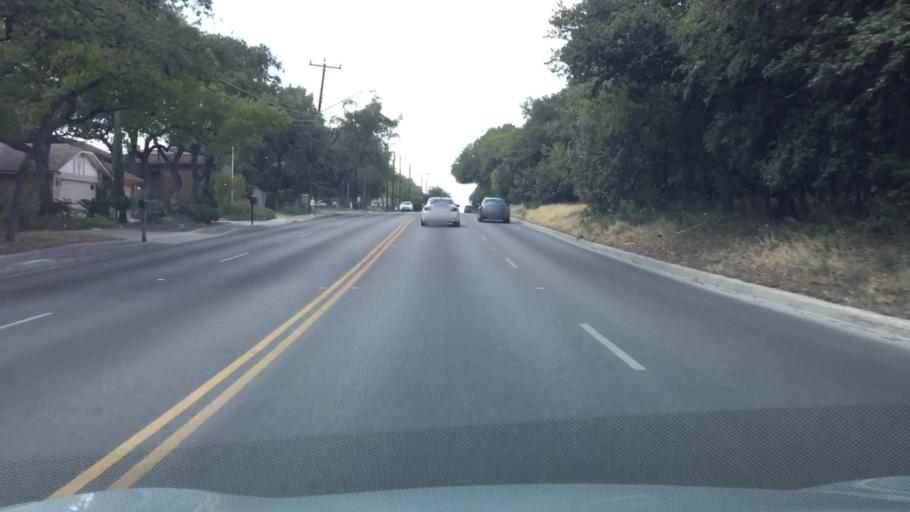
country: US
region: Texas
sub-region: Bexar County
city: Hollywood Park
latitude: 29.5589
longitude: -98.4748
